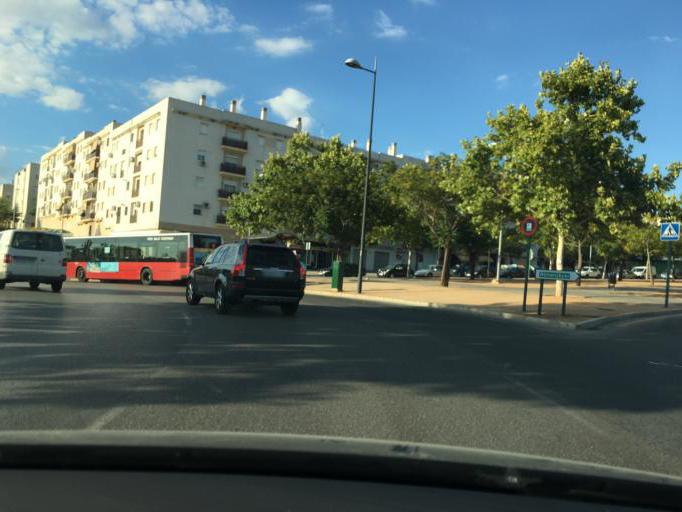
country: ES
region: Andalusia
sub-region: Provincia de Granada
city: Maracena
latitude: 37.2063
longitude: -3.6190
